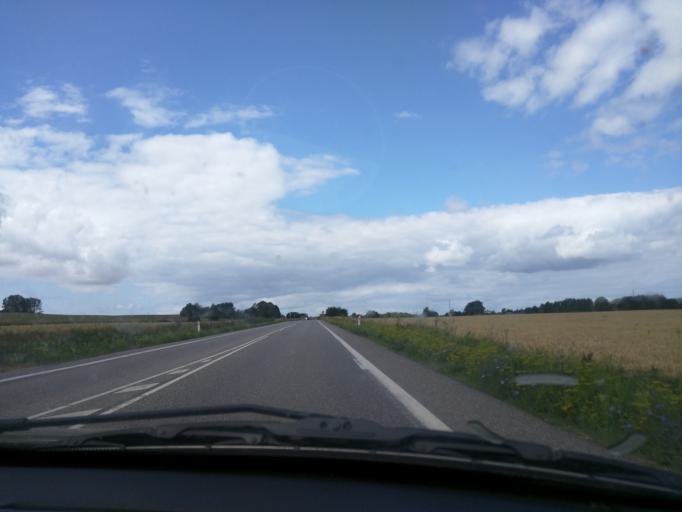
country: DK
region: Zealand
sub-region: Kalundborg Kommune
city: Svebolle
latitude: 55.6646
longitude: 11.2499
